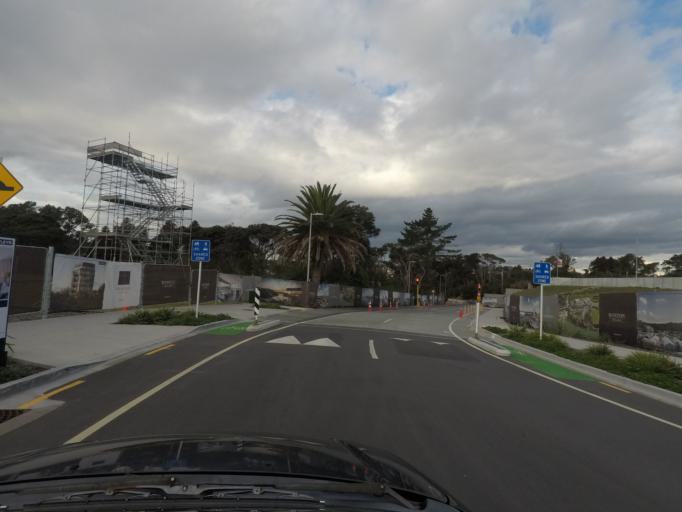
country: NZ
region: Auckland
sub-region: Auckland
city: North Shore
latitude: -36.7890
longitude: 174.6697
